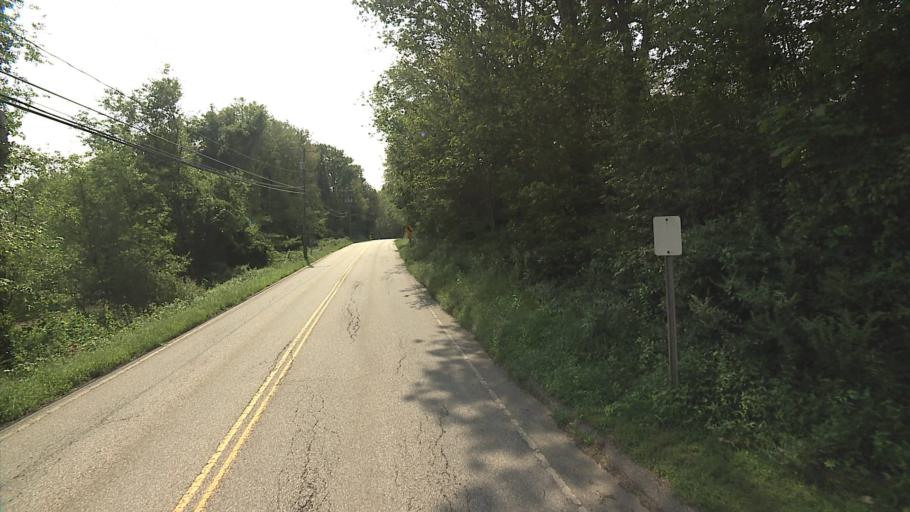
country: US
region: Connecticut
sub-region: Middlesex County
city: East Haddam
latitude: 41.4617
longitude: -72.4420
